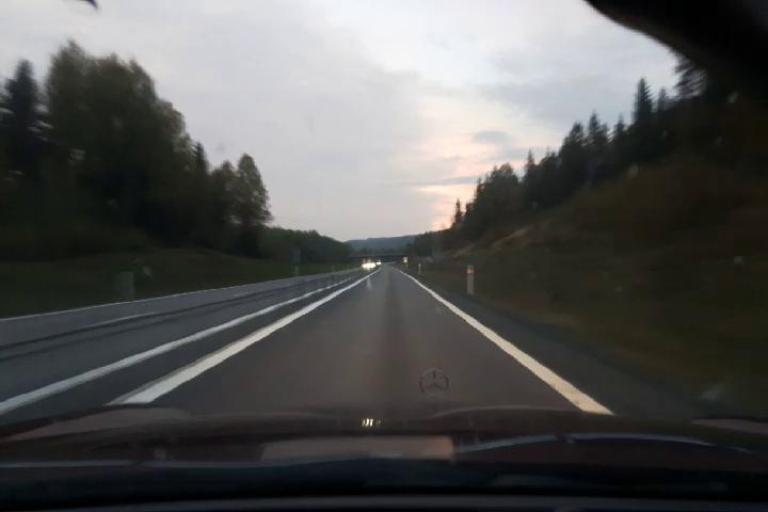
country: SE
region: Vaesternorrland
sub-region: Kramfors Kommun
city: Nordingra
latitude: 62.9352
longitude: 18.0942
